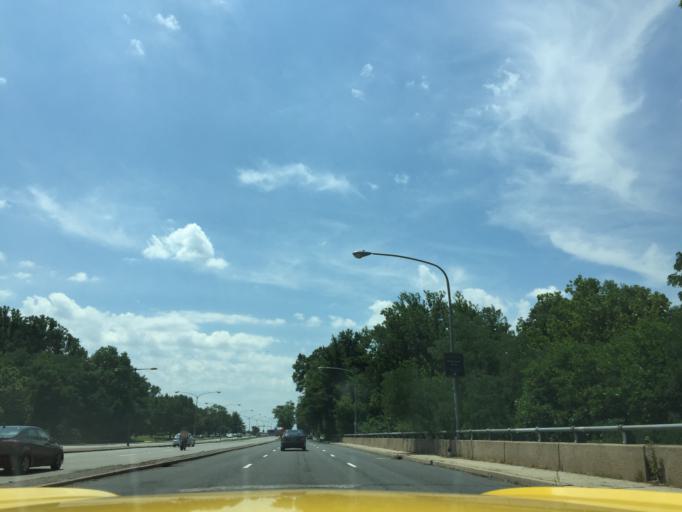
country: US
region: Pennsylvania
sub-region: Montgomery County
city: Rockledge
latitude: 40.0666
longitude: -75.0411
